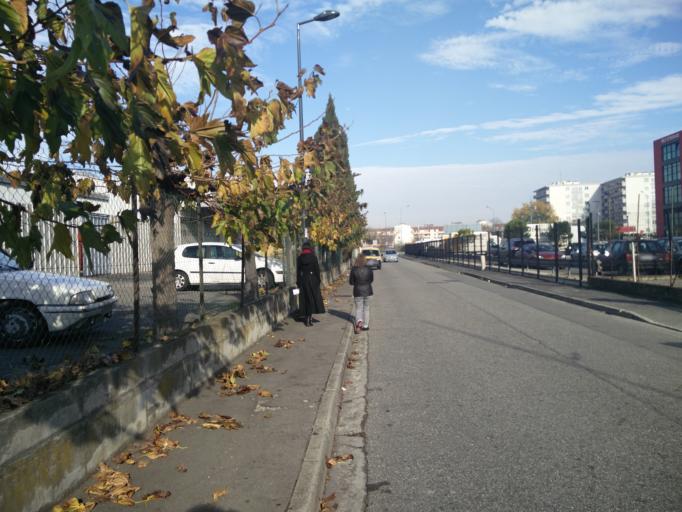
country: FR
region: Midi-Pyrenees
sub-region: Departement de la Haute-Garonne
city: Toulouse
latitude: 43.5725
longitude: 1.4086
